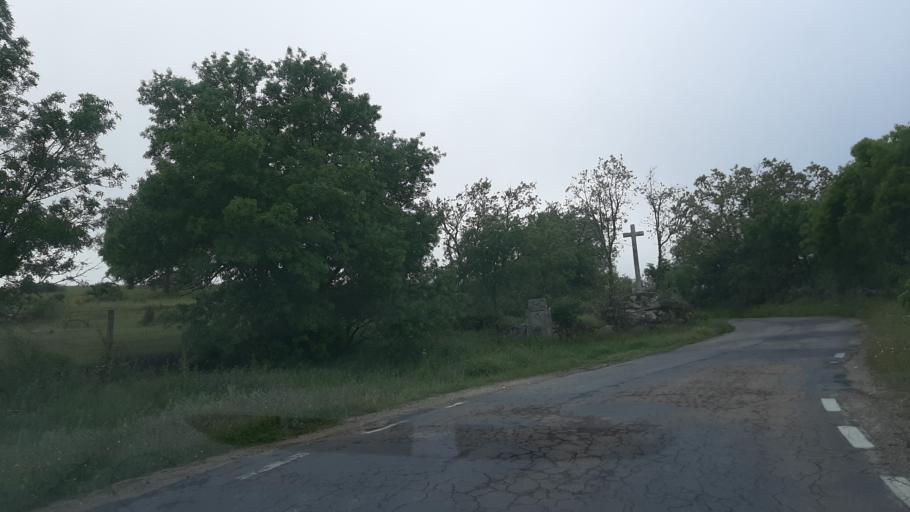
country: ES
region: Castille and Leon
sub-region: Provincia de Salamanca
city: Endrinal
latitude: 40.5516
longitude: -5.8045
